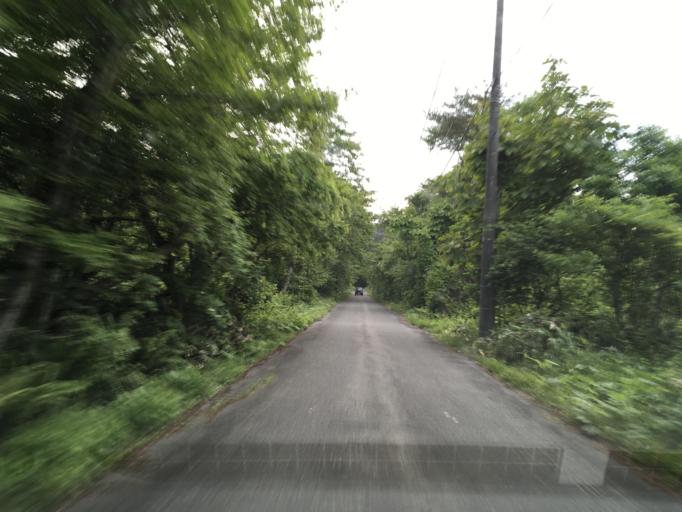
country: JP
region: Iwate
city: Mizusawa
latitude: 39.1363
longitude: 141.3072
